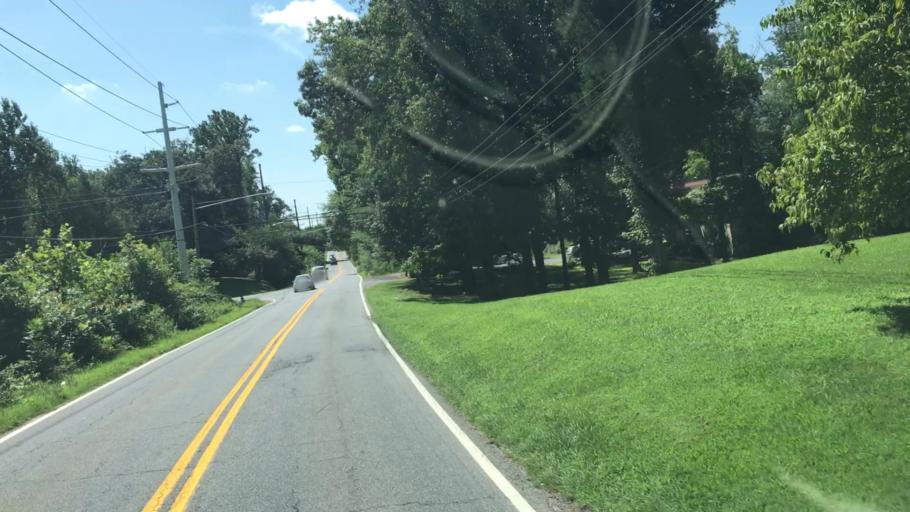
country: US
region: Maryland
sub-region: Prince George's County
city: Brandywine
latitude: 38.7126
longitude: -76.8850
